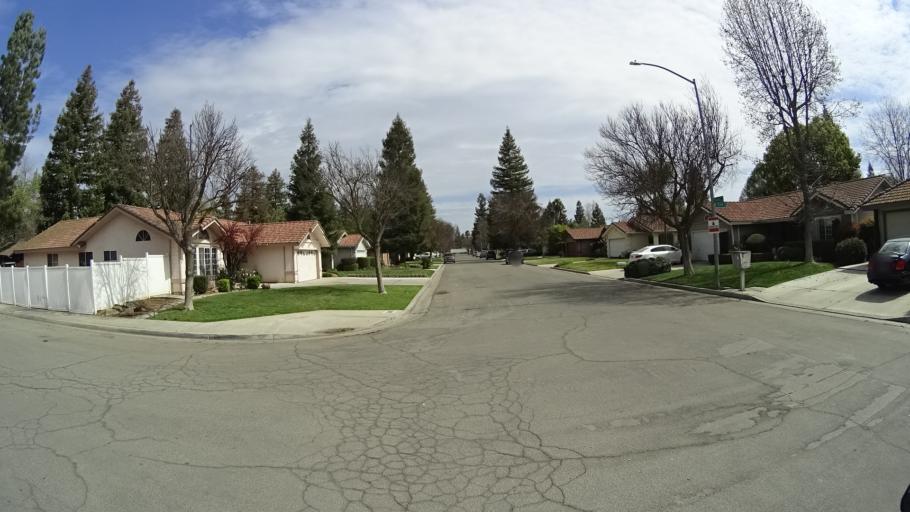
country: US
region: California
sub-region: Fresno County
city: Biola
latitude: 36.8401
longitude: -119.8999
